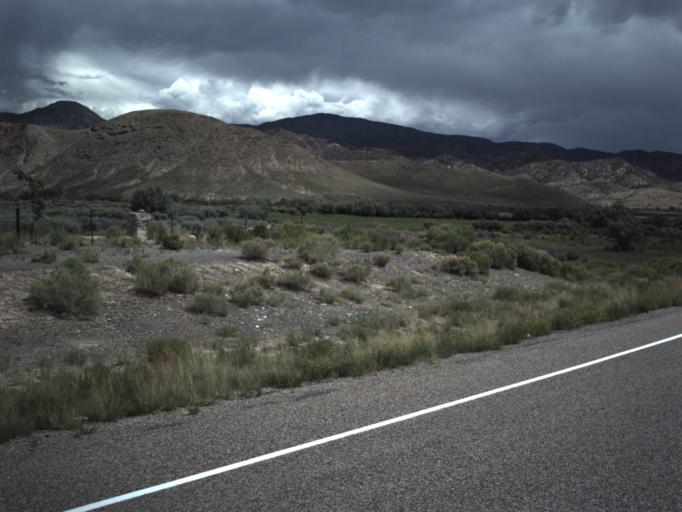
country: US
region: Utah
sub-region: Piute County
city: Junction
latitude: 38.2086
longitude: -112.2136
